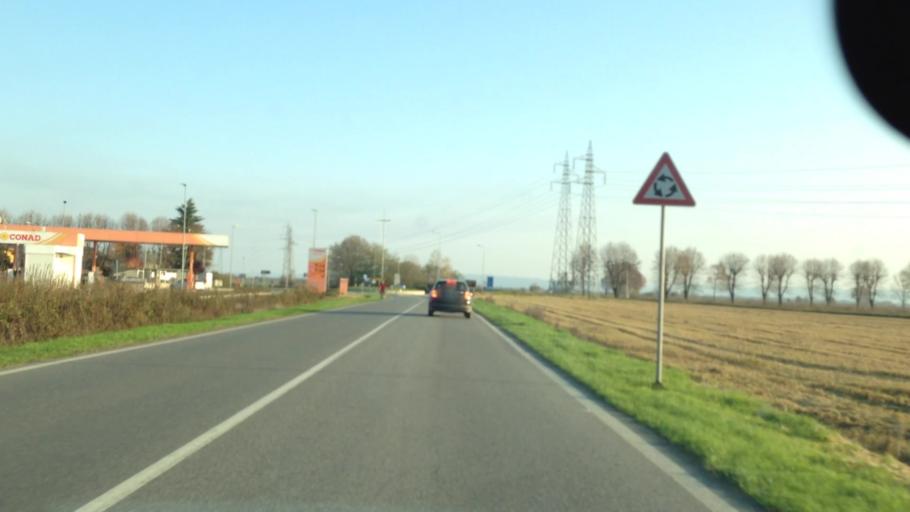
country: IT
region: Piedmont
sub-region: Provincia di Vercelli
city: Livorno Ferraris
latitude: 45.2749
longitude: 8.0746
